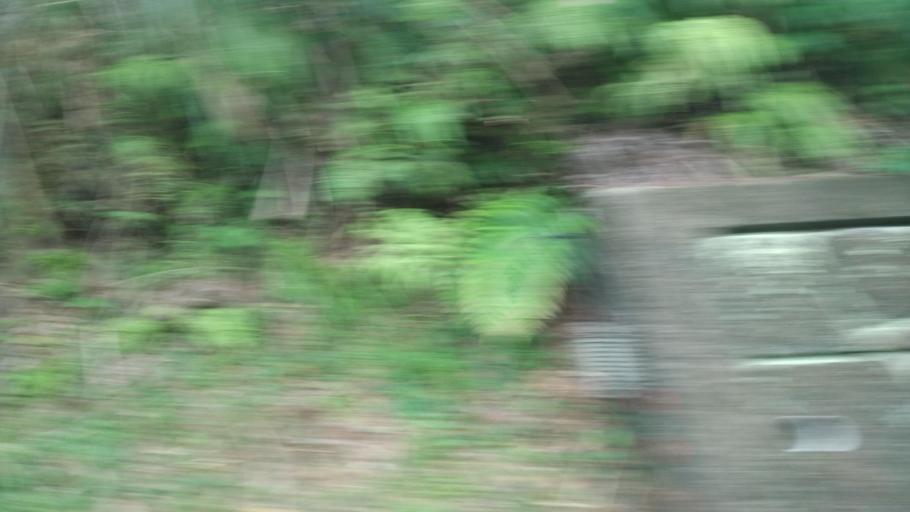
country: TW
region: Taipei
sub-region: Taipei
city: Banqiao
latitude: 24.9387
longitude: 121.4688
